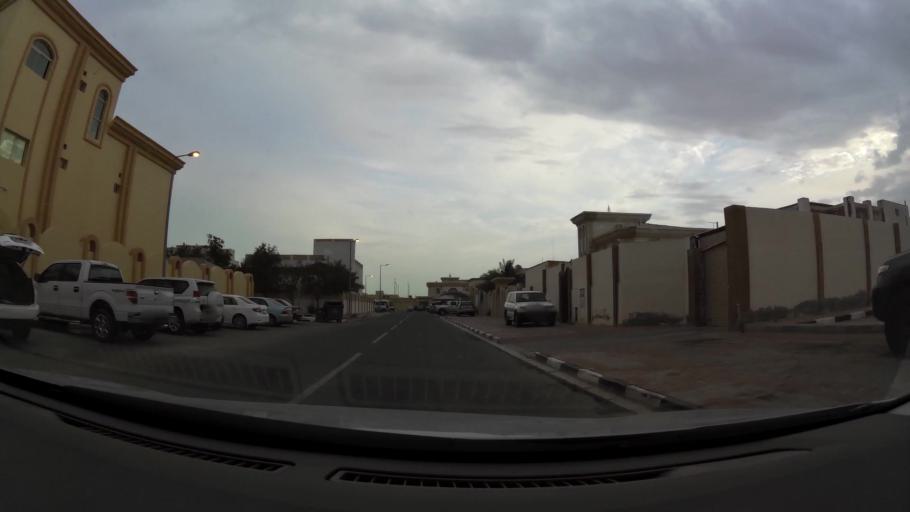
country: QA
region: Baladiyat ad Dawhah
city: Doha
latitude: 25.3385
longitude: 51.5092
